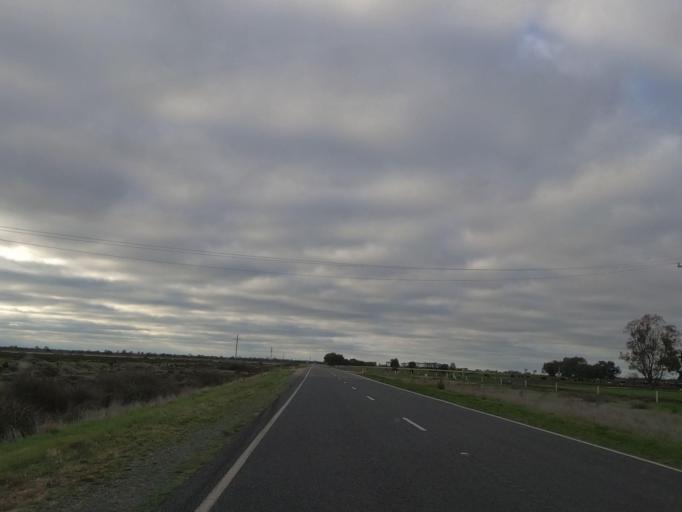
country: AU
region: Victoria
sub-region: Swan Hill
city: Swan Hill
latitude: -35.8352
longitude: 143.9422
